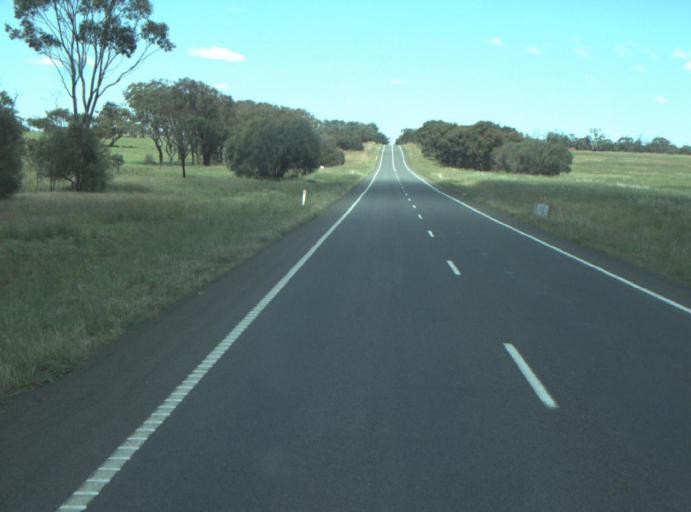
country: AU
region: Victoria
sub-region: Greater Geelong
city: Lara
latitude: -37.9096
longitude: 144.3688
